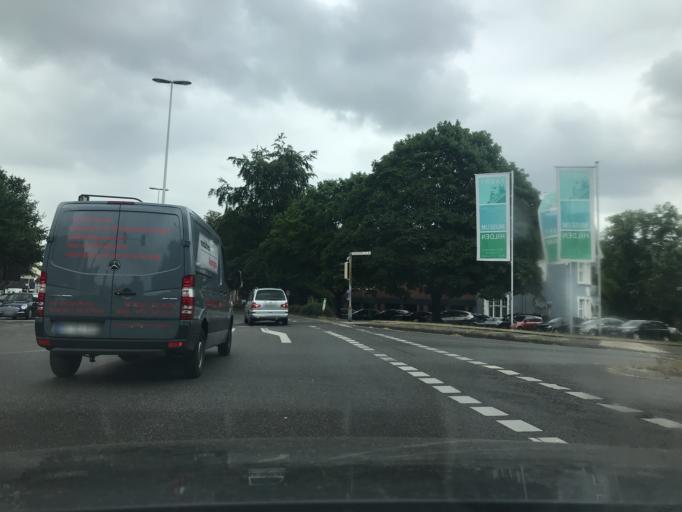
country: DE
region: North Rhine-Westphalia
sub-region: Regierungsbezirk Dusseldorf
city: Hilden
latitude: 51.1694
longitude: 6.9441
